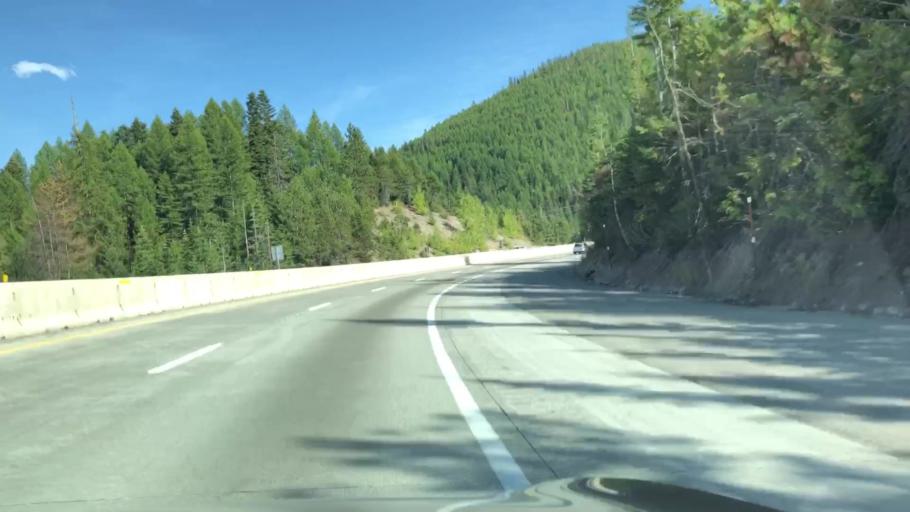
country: US
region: Idaho
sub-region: Shoshone County
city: Wallace
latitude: 47.4624
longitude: -115.6965
